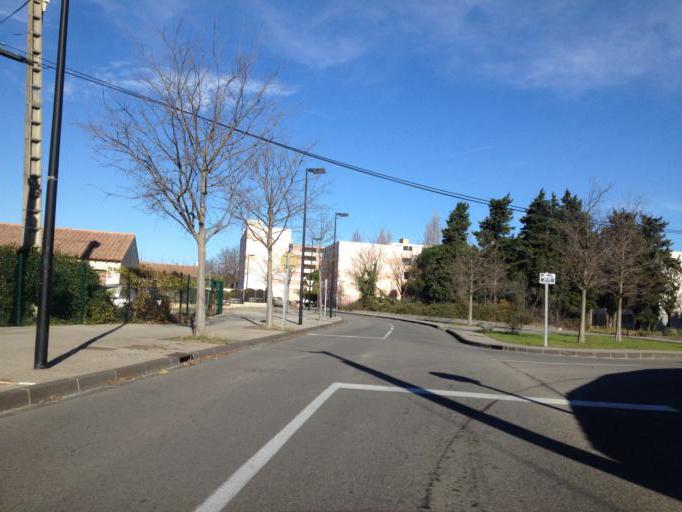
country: FR
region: Provence-Alpes-Cote d'Azur
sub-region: Departement du Vaucluse
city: Orange
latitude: 44.1536
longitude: 4.7991
